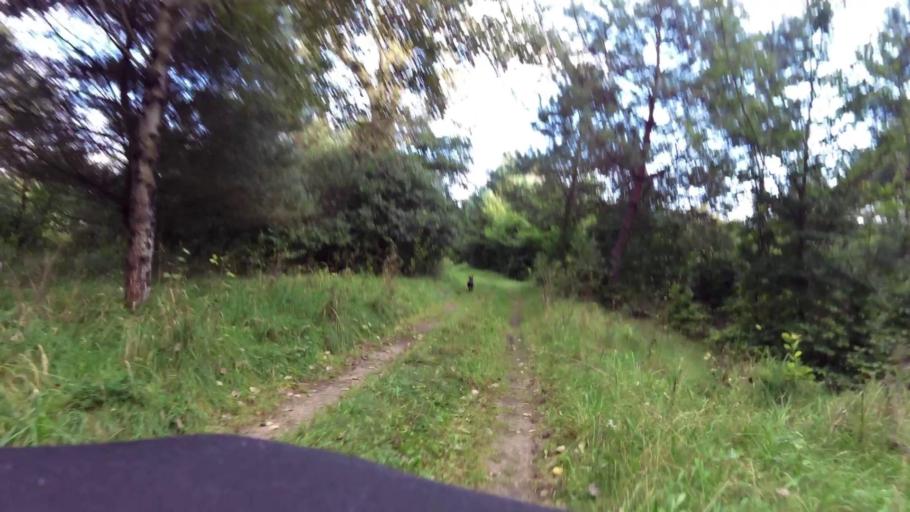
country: PL
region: West Pomeranian Voivodeship
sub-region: Powiat stargardzki
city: Marianowo
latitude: 53.3832
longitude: 15.3453
